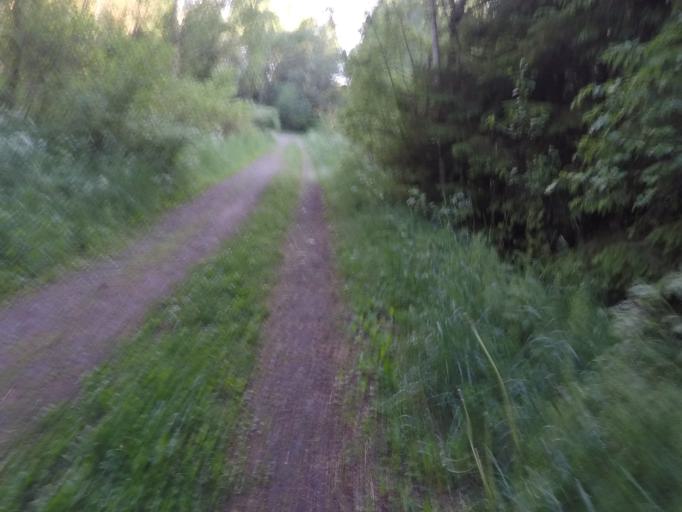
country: SE
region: Soedermanland
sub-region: Eskilstuna Kommun
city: Hallbybrunn
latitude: 59.3984
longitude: 16.3975
